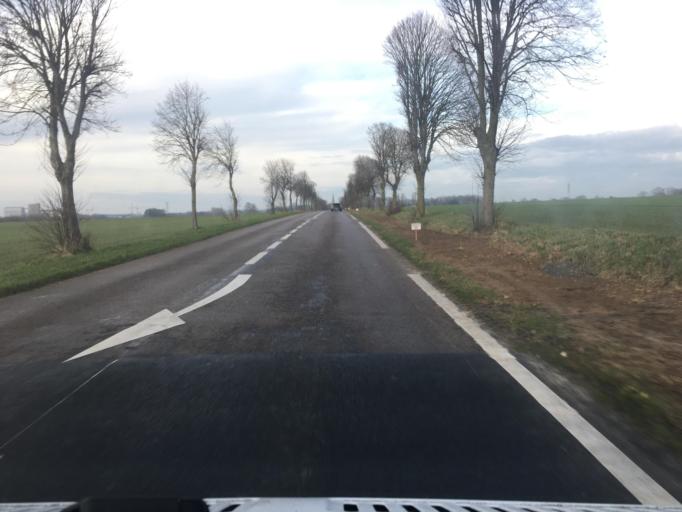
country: FR
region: Lower Normandy
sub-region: Departement du Calvados
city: Rots
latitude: 49.2050
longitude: -0.4939
